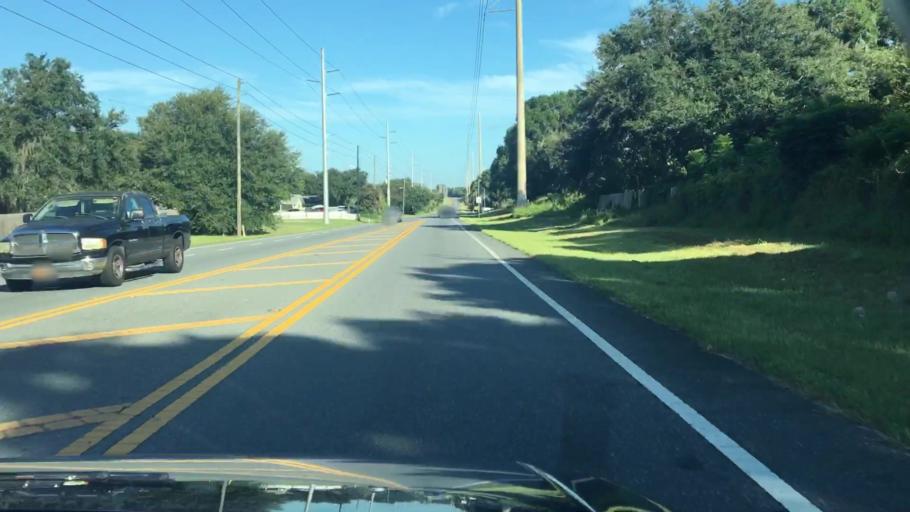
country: US
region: Florida
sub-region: Lake County
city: Eustis
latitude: 28.8774
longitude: -81.7113
